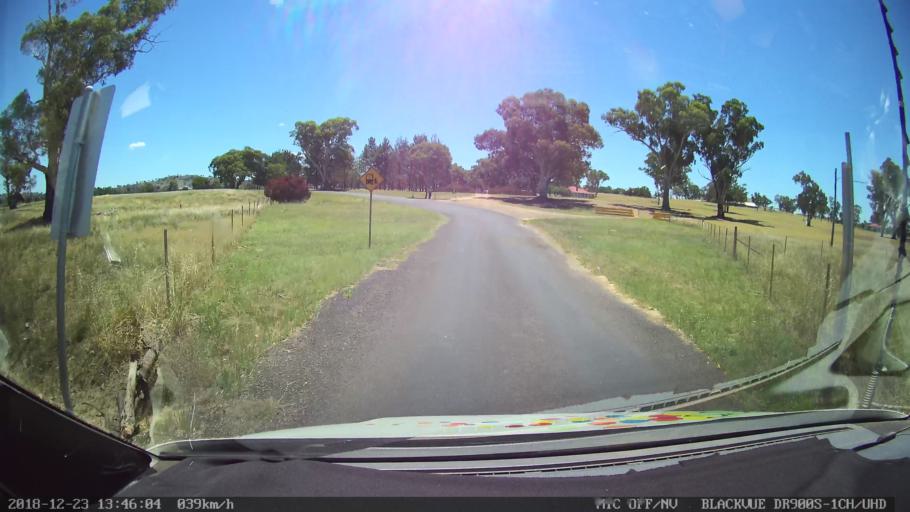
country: AU
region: New South Wales
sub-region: Tamworth Municipality
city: Manilla
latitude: -30.5044
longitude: 151.1221
